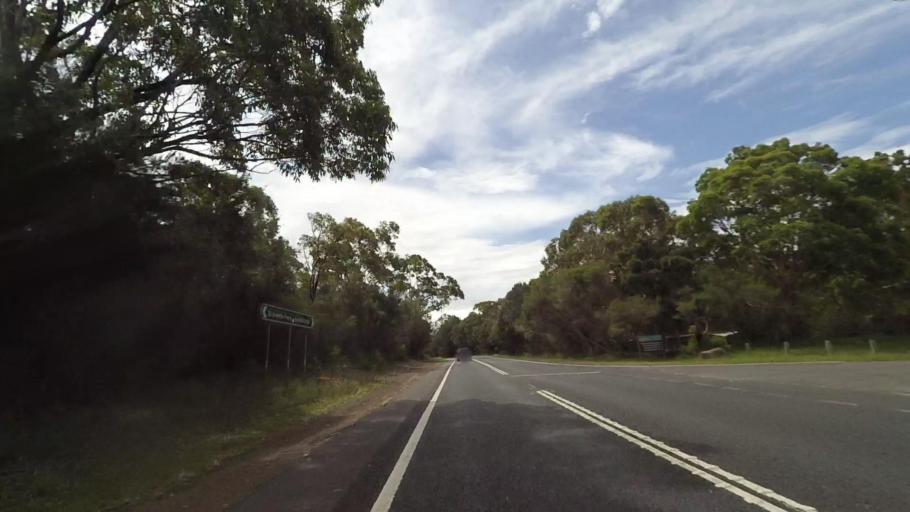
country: AU
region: New South Wales
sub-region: Sutherland Shire
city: Loftus
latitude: -34.0633
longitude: 151.0567
